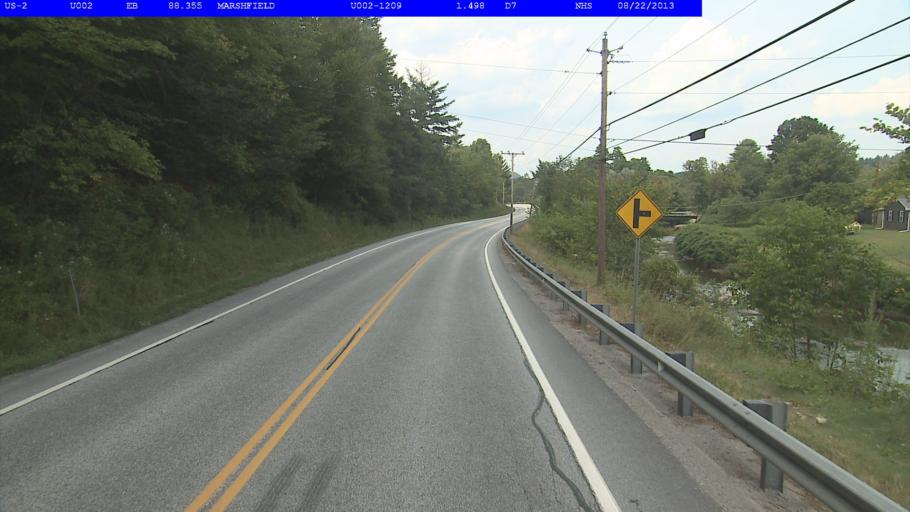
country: US
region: Vermont
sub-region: Washington County
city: Barre
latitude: 44.2926
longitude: -72.3989
